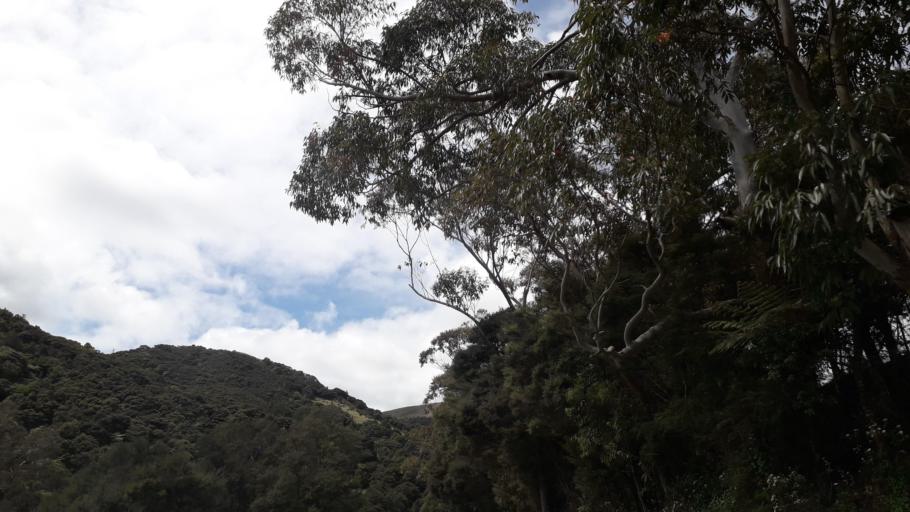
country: NZ
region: Northland
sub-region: Far North District
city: Taipa
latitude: -35.0935
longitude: 173.5277
